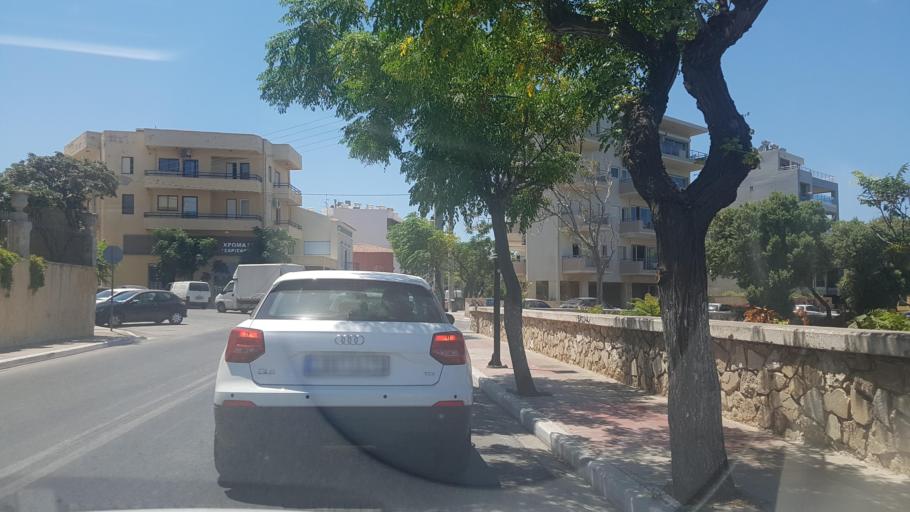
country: GR
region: Crete
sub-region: Nomos Chanias
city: Chania
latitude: 35.5165
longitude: 24.0322
